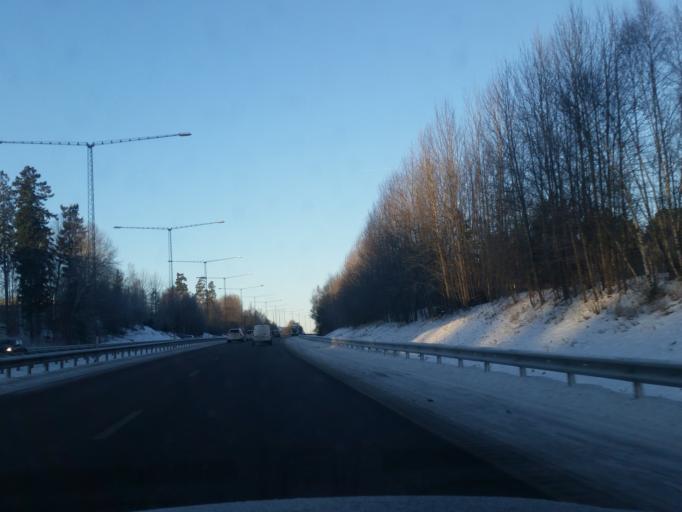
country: SE
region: Stockholm
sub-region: Sodertalje Kommun
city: Soedertaelje
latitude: 59.1767
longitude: 17.6229
